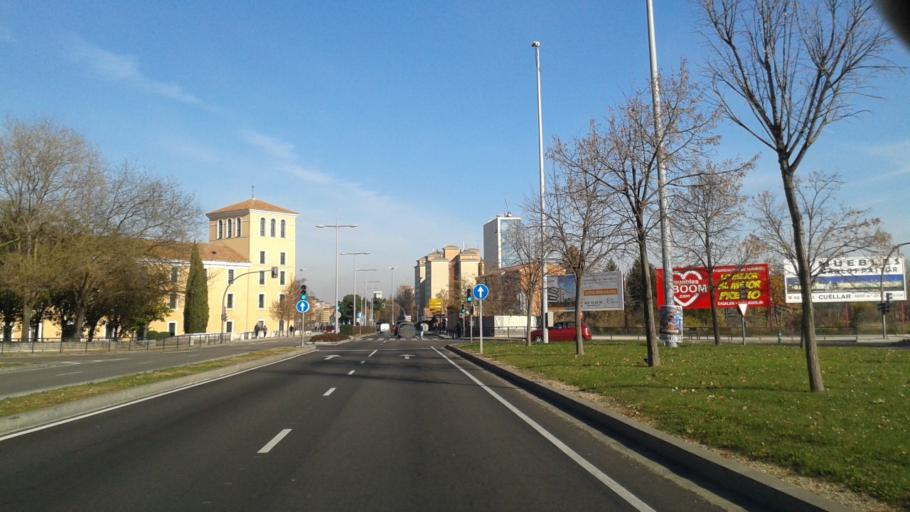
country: ES
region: Castille and Leon
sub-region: Provincia de Valladolid
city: Valladolid
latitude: 41.6391
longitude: -4.7456
